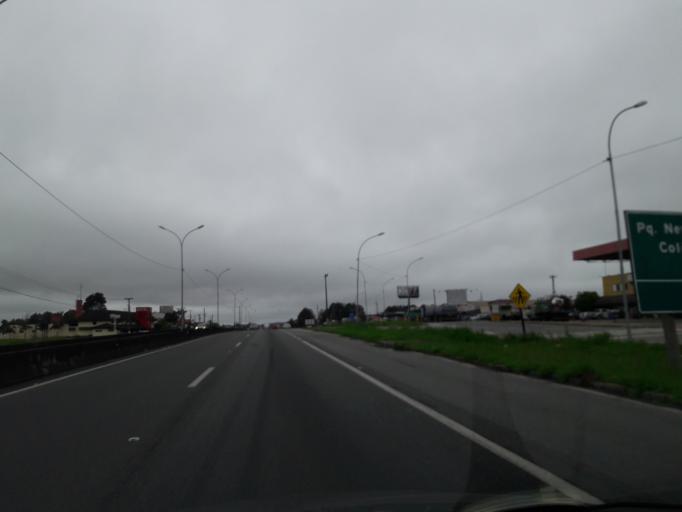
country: BR
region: Parana
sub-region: Quatro Barras
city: Quatro Barras
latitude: -25.3723
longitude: -49.1375
